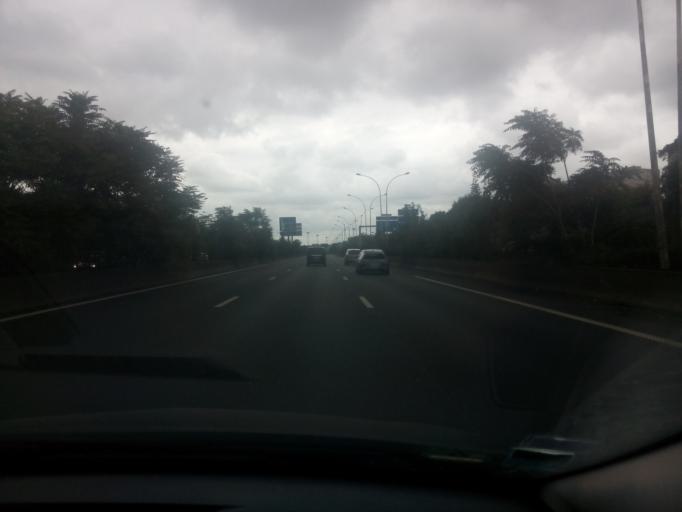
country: FR
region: Ile-de-France
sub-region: Departement du Val-de-Marne
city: Chevilly-Larue
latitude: 48.7770
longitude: 2.3461
